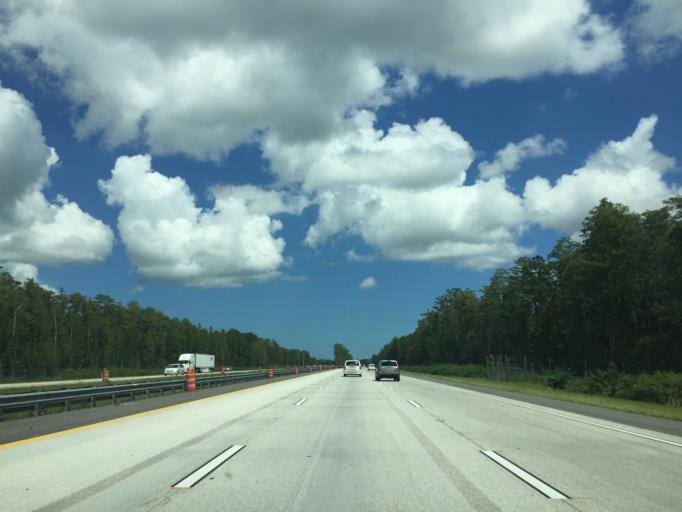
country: US
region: Florida
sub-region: Volusia County
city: Samsula-Spruce Creek
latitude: 29.0857
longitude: -81.1670
